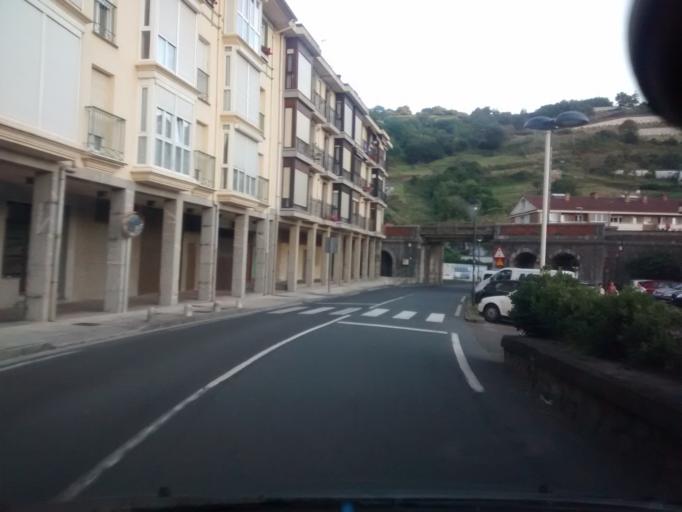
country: ES
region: Basque Country
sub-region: Provincia de Guipuzcoa
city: Deba
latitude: 43.2979
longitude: -2.3504
